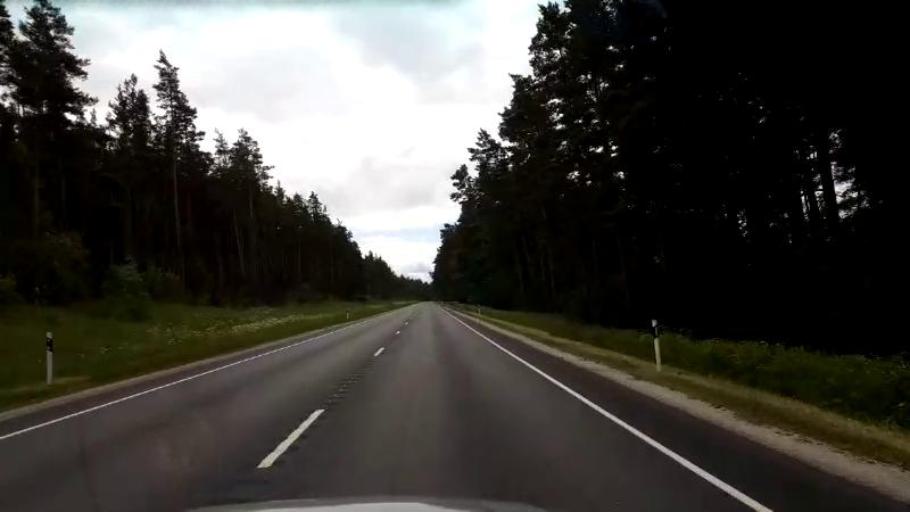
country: EE
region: Paernumaa
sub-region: Paernu linn
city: Parnu
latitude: 58.1582
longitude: 24.4984
